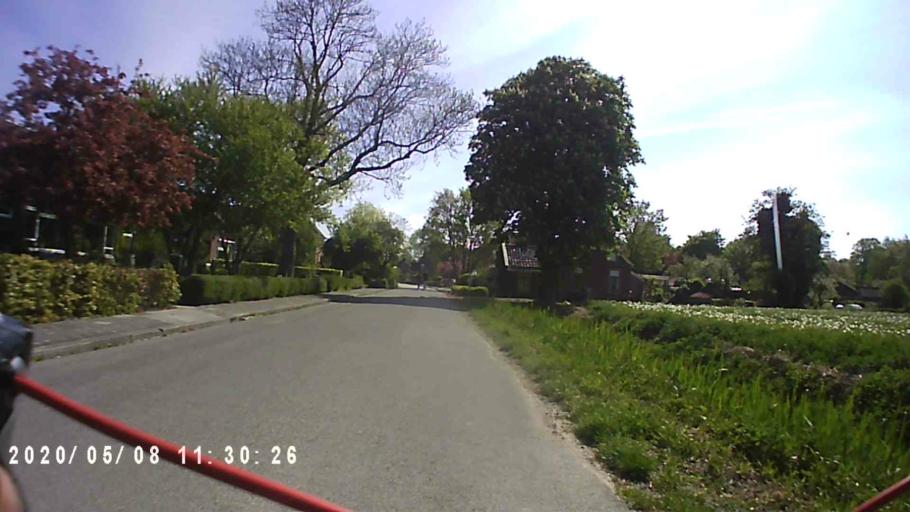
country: NL
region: Groningen
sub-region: Gemeente Bedum
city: Bedum
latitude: 53.3457
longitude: 6.7077
